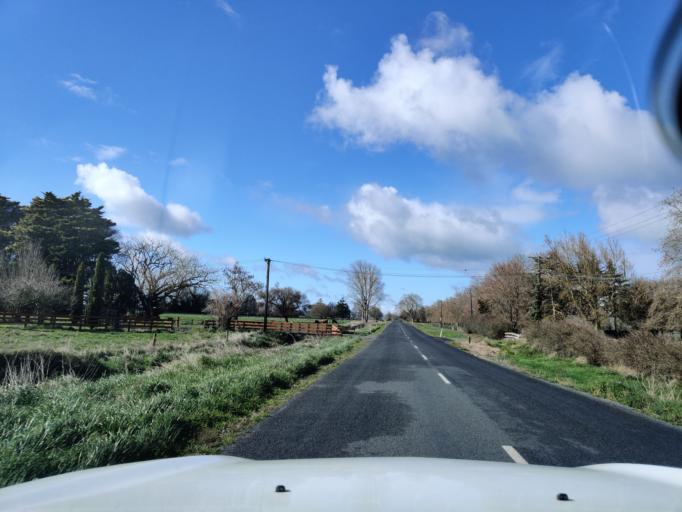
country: NZ
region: Waikato
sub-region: Waikato District
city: Ngaruawahia
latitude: -37.6096
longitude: 175.3087
